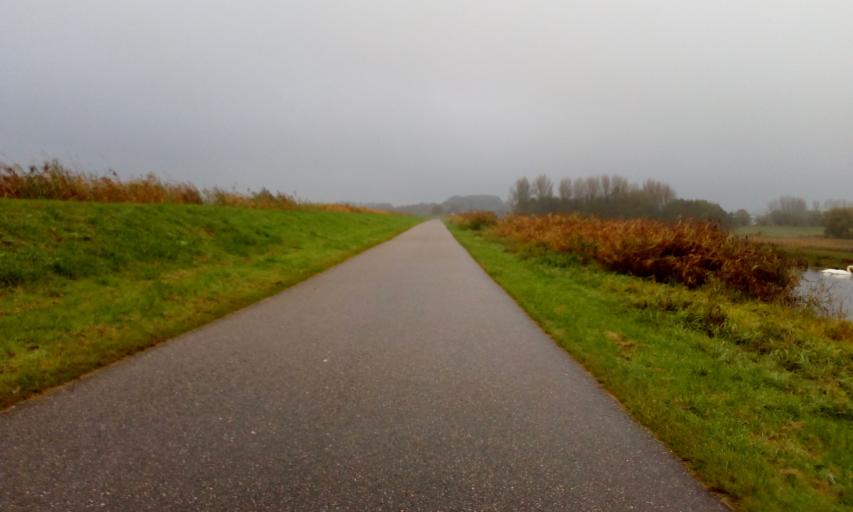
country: NL
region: South Holland
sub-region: Gemeente Lansingerland
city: Bleiswijk
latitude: 51.9877
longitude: 4.5470
